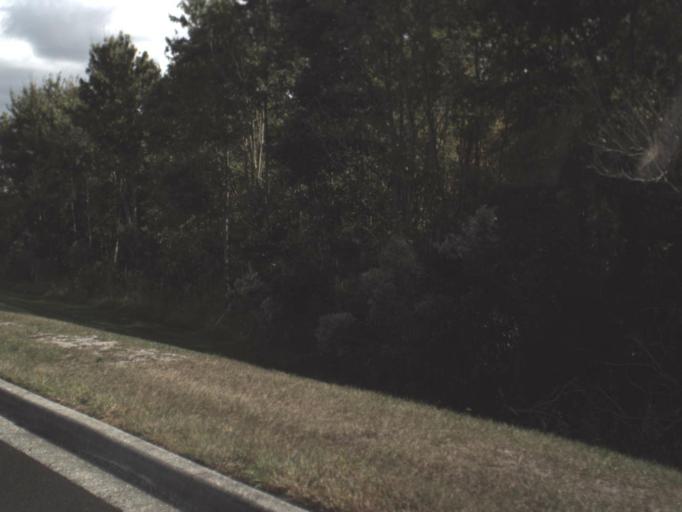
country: US
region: Florida
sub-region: Orange County
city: Hunters Creek
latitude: 28.3454
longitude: -81.4653
